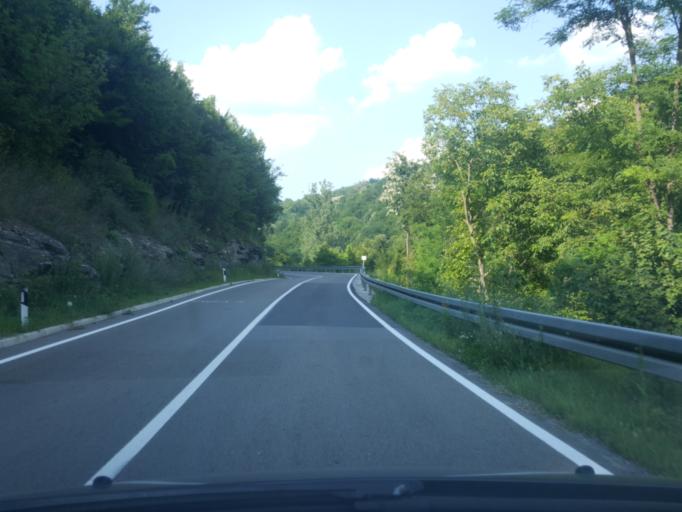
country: RS
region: Central Serbia
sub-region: Moravicki Okrug
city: Gornji Milanovac
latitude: 44.1619
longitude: 20.5117
